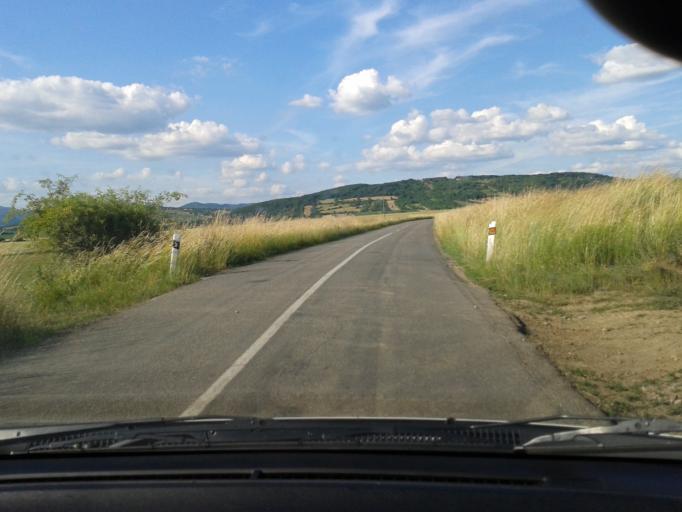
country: SK
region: Nitriansky
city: Levice
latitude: 48.2892
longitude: 18.7567
